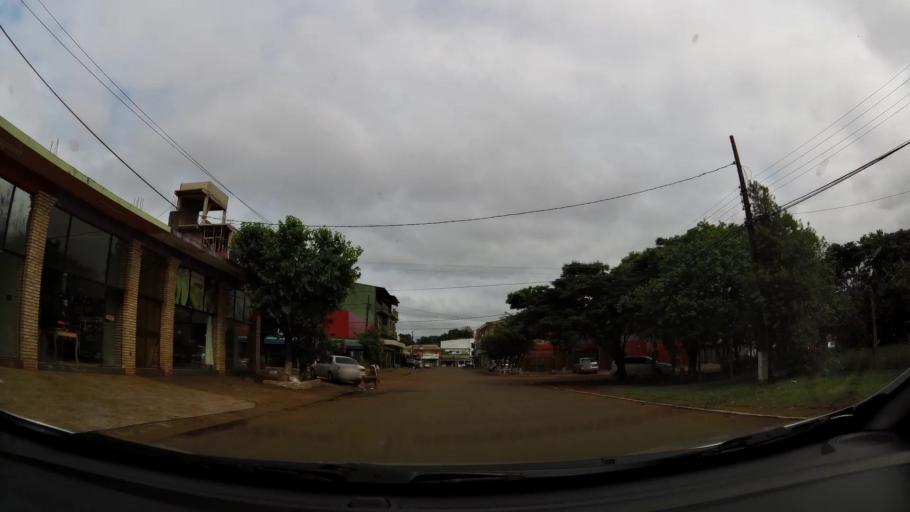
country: PY
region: Alto Parana
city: Ciudad del Este
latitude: -25.3948
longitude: -54.6400
